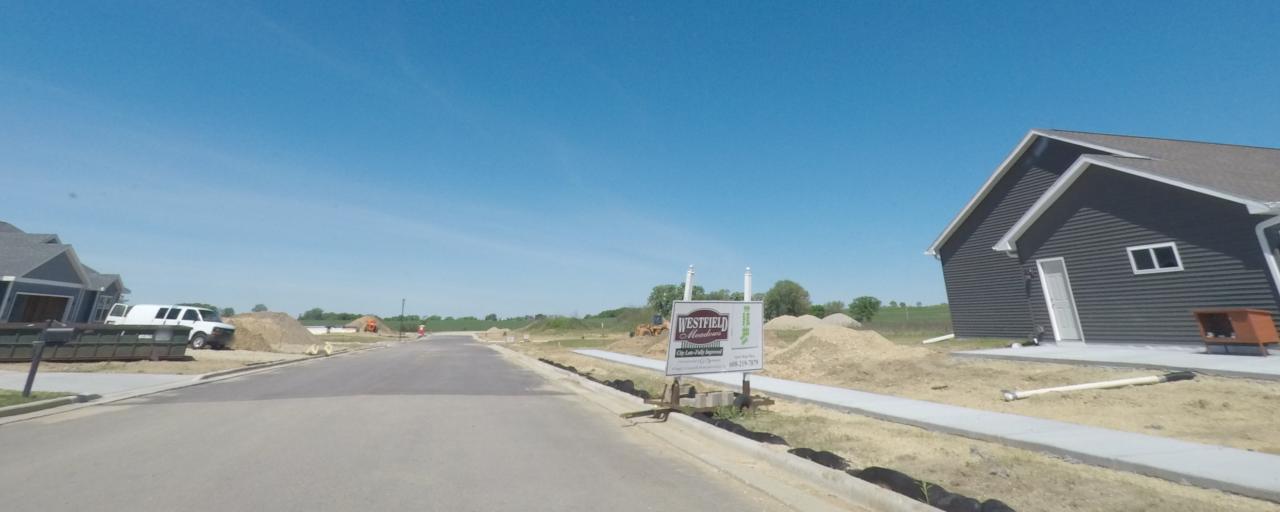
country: US
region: Wisconsin
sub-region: Rock County
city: Evansville
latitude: 42.7744
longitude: -89.3212
